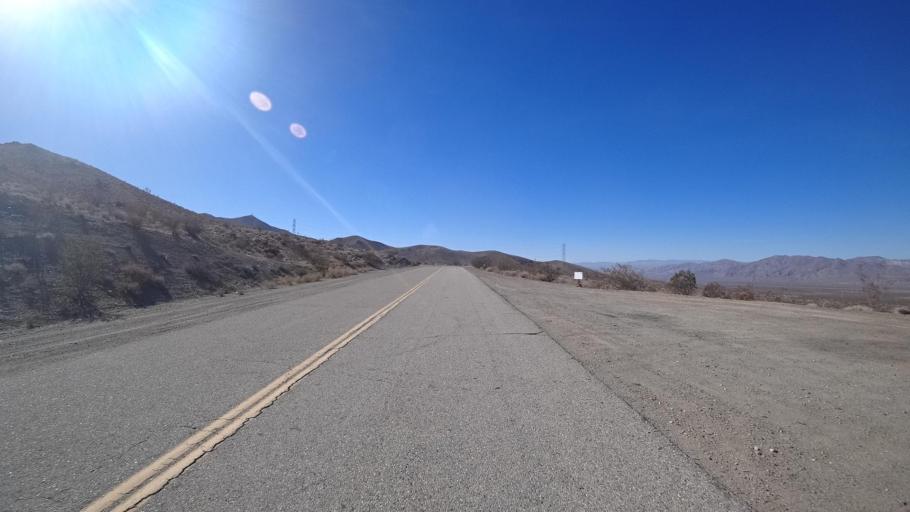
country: US
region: California
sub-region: Kern County
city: Ridgecrest
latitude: 35.3786
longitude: -117.6517
